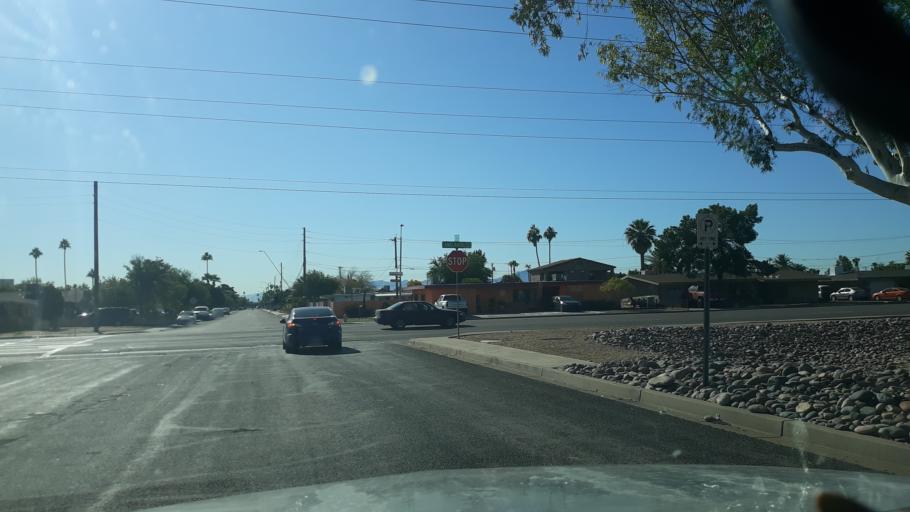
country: US
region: Arizona
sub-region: Maricopa County
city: Glendale
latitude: 33.5099
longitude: -112.1732
